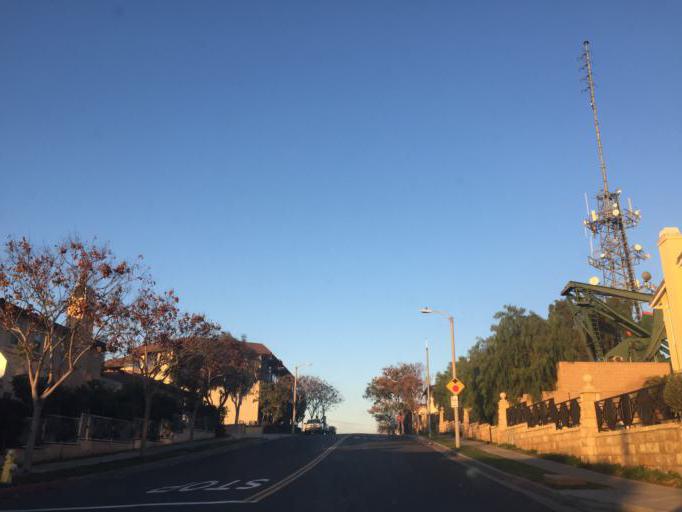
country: US
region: California
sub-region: Los Angeles County
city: Signal Hill
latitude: 33.7989
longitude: -118.1621
